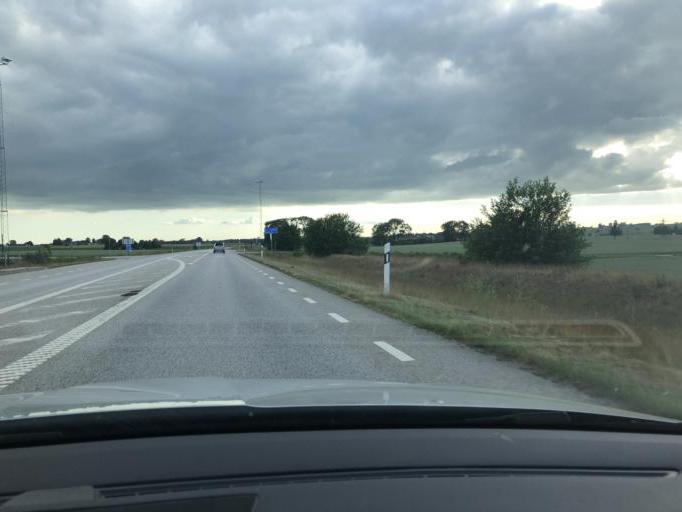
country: SE
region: Skane
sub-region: Simrishamns Kommun
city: Simrishamn
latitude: 55.5386
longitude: 14.3201
